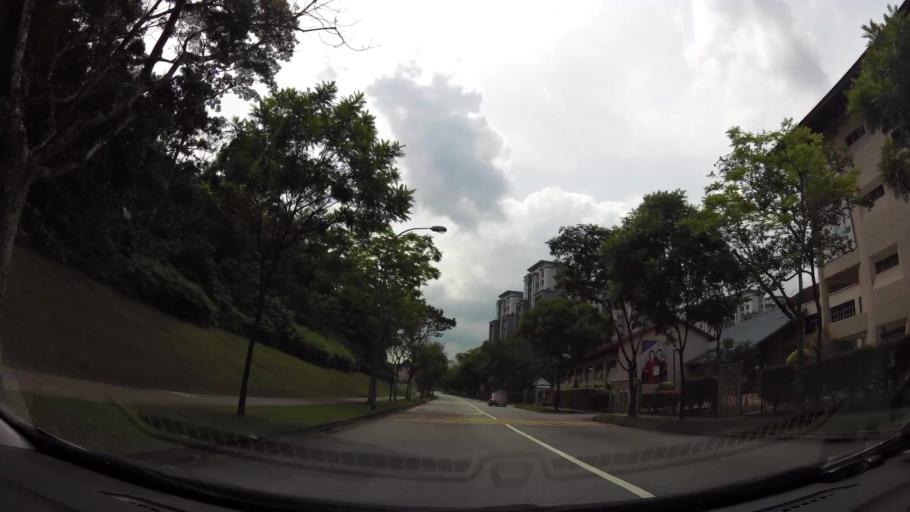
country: SG
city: Singapore
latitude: 1.3432
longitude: 103.7610
